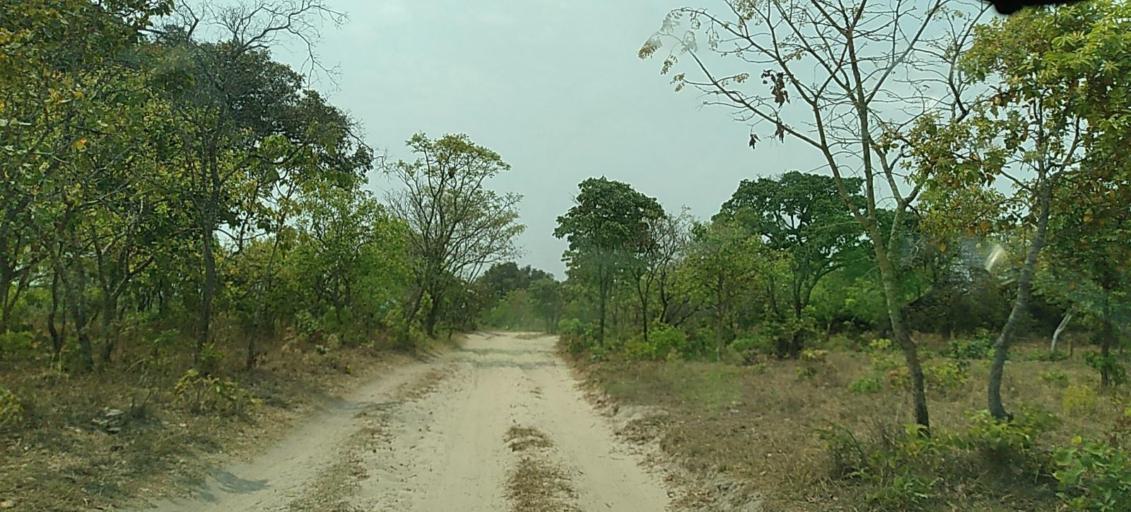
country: ZM
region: North-Western
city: Kabompo
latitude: -13.4768
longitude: 24.4562
